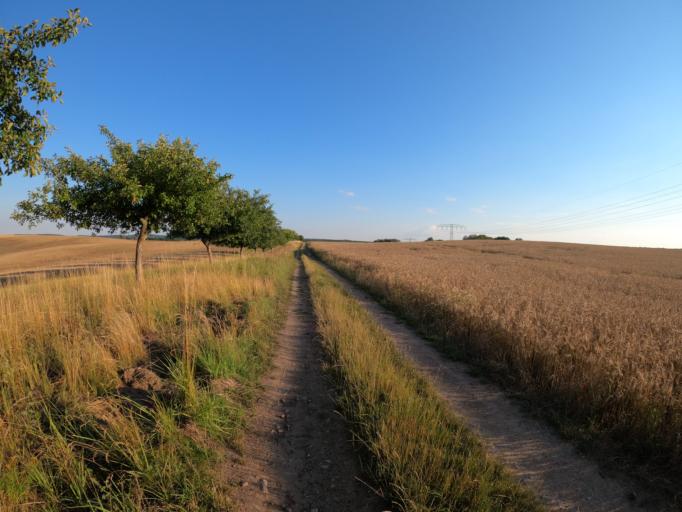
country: DE
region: Brandenburg
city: Althuttendorf
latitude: 53.0336
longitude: 13.8673
